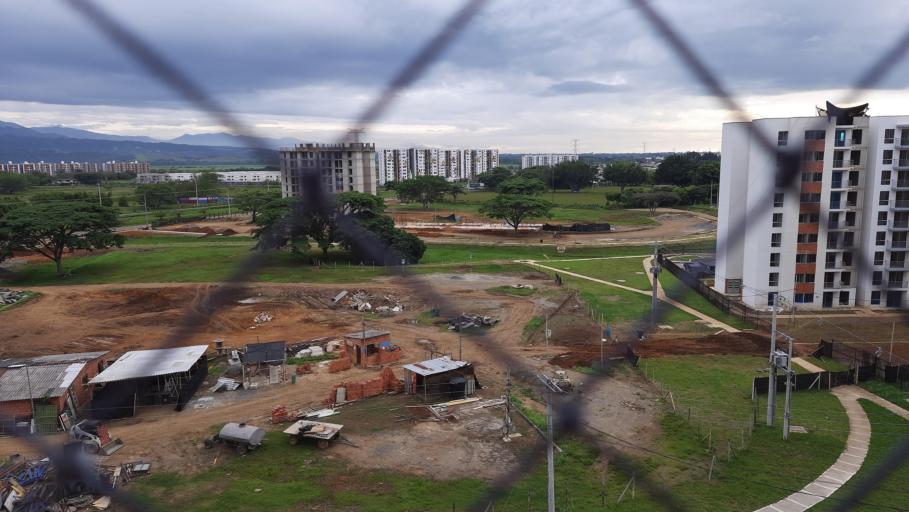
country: CO
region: Valle del Cauca
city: Jamundi
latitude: 3.2596
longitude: -76.5483
